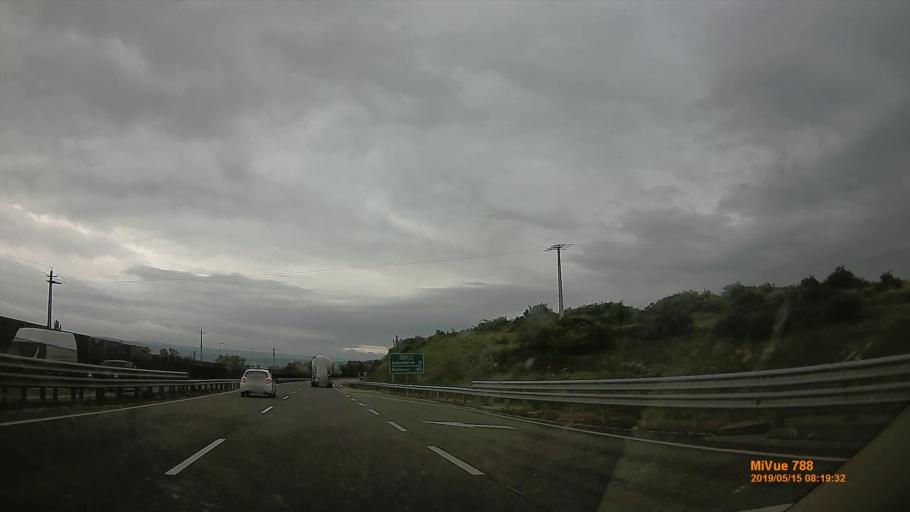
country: HU
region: Veszprem
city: Petfuerdo
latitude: 47.1591
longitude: 18.0804
